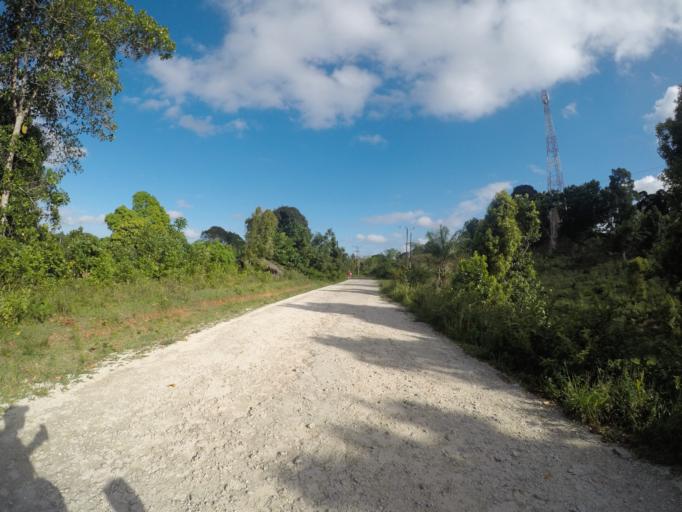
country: TZ
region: Pemba South
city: Mtambile
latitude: -5.3523
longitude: 39.7049
